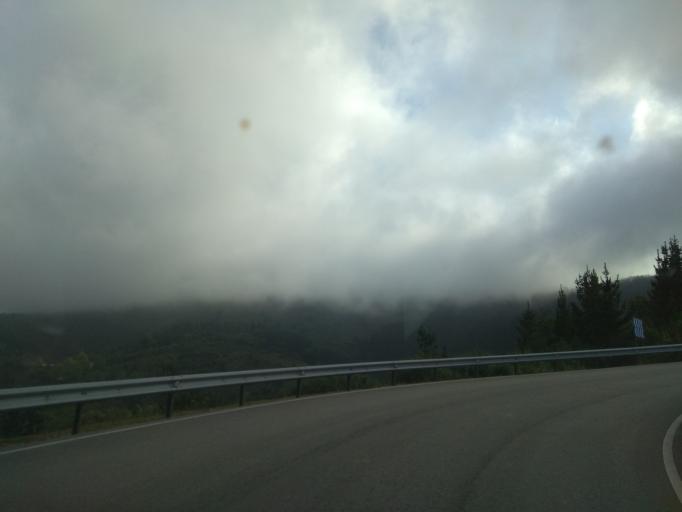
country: ES
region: Cantabria
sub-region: Provincia de Cantabria
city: San Vicente de la Barquera
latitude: 43.3086
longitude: -4.3993
